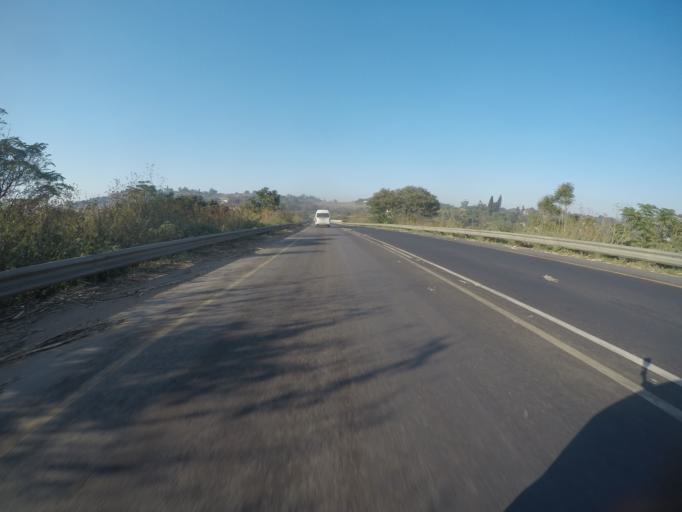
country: ZA
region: KwaZulu-Natal
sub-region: iLembe District Municipality
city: Stanger
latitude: -29.3819
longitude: 31.2527
